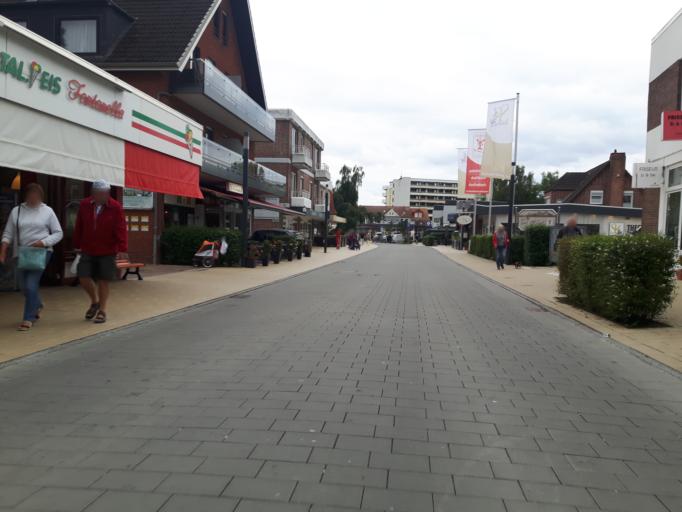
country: DE
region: Schleswig-Holstein
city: Gromitz
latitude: 54.1473
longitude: 10.9609
